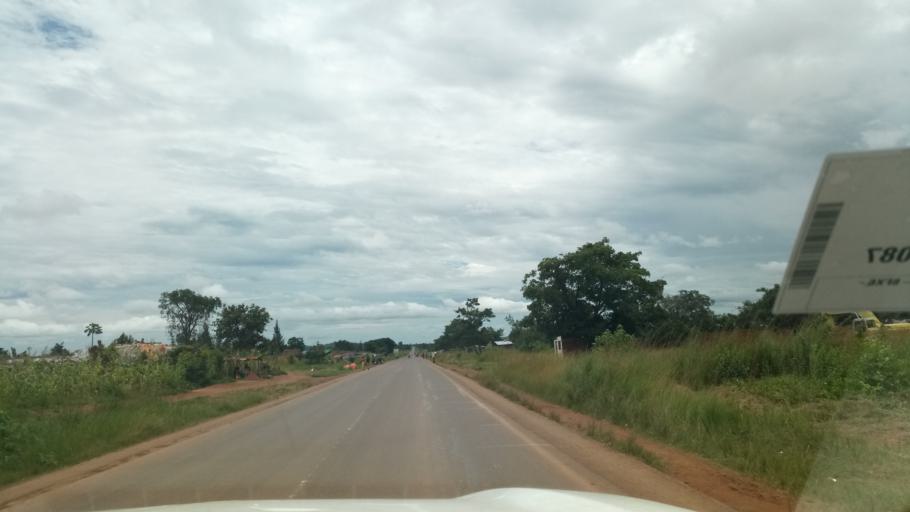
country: CD
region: Katanga
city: Lubumbashi
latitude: -11.5699
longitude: 27.5479
